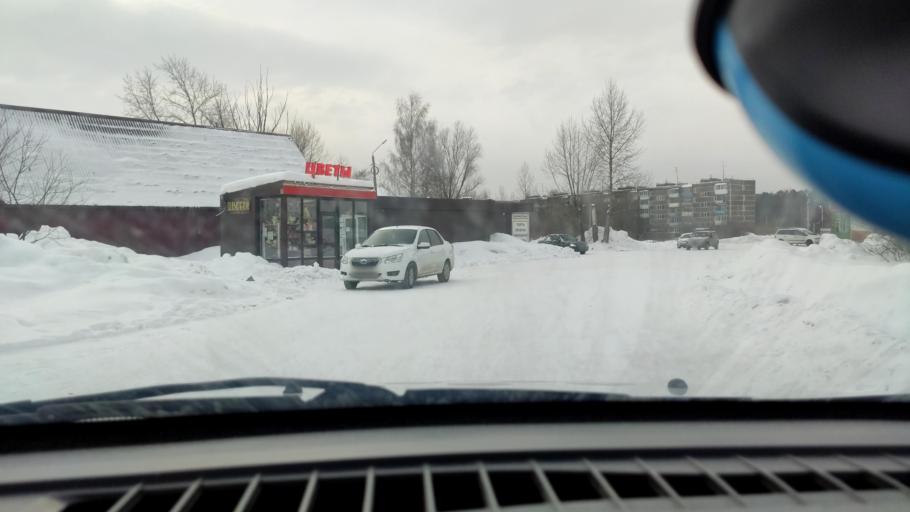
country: RU
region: Perm
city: Overyata
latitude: 58.0807
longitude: 55.8730
